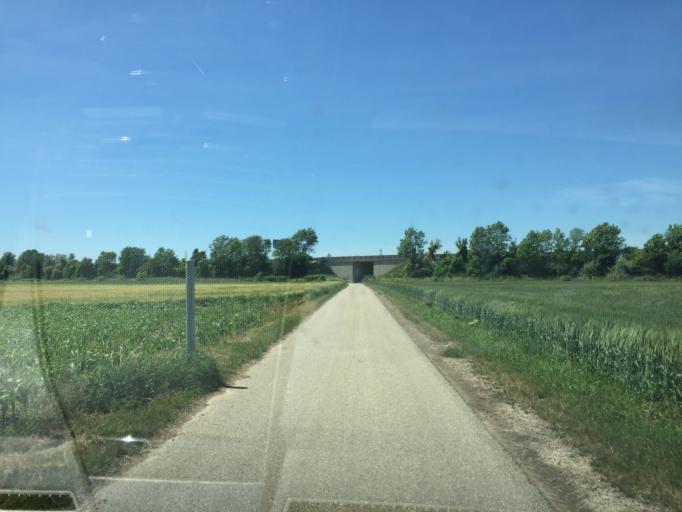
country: AT
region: Lower Austria
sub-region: Politischer Bezirk Sankt Polten
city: Herzogenburg
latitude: 48.2358
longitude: 15.6845
